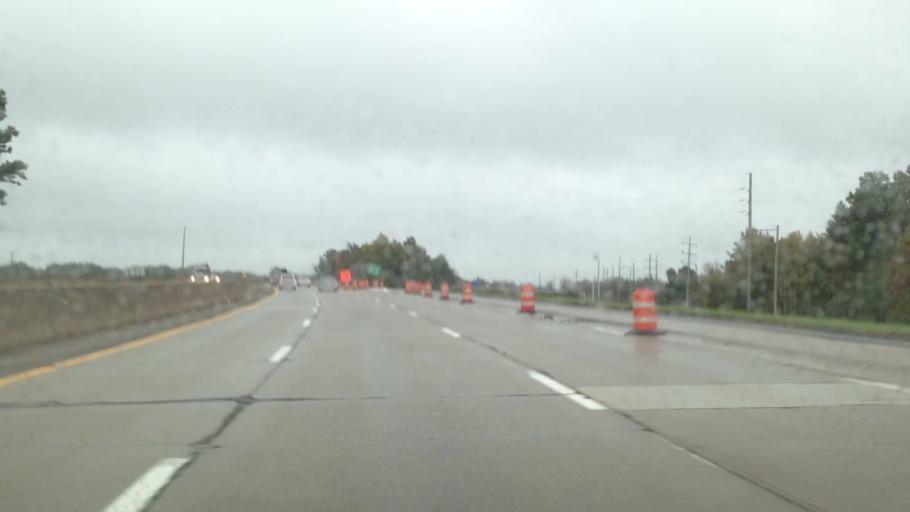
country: US
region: Ohio
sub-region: Summit County
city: Boston Heights
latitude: 41.2371
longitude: -81.4940
